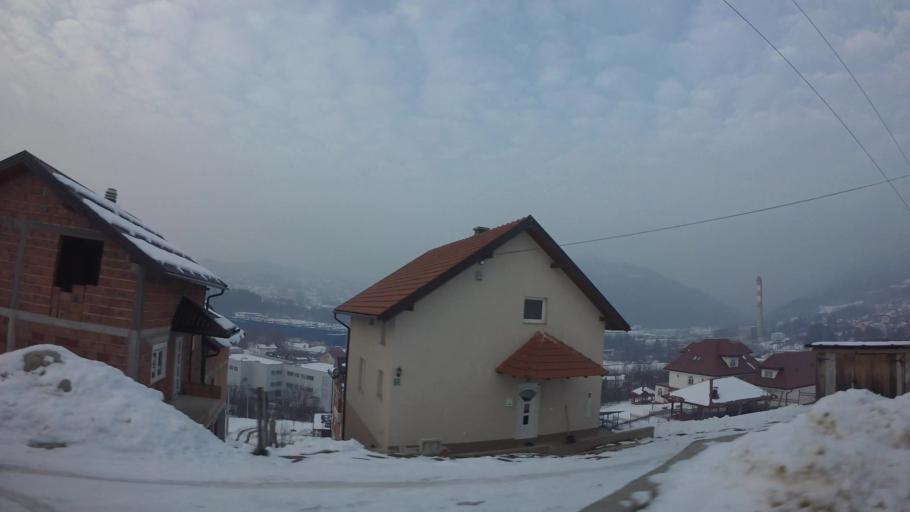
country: BA
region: Federation of Bosnia and Herzegovina
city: Hotonj
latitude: 43.8959
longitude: 18.3645
